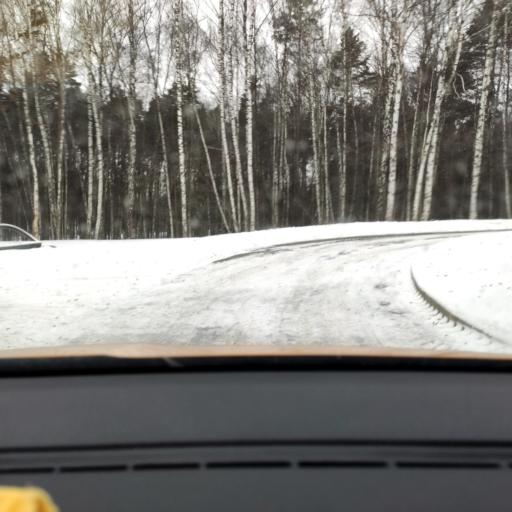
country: RU
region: Moskovskaya
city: Bol'shaya Setun'
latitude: 55.7496
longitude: 37.3963
